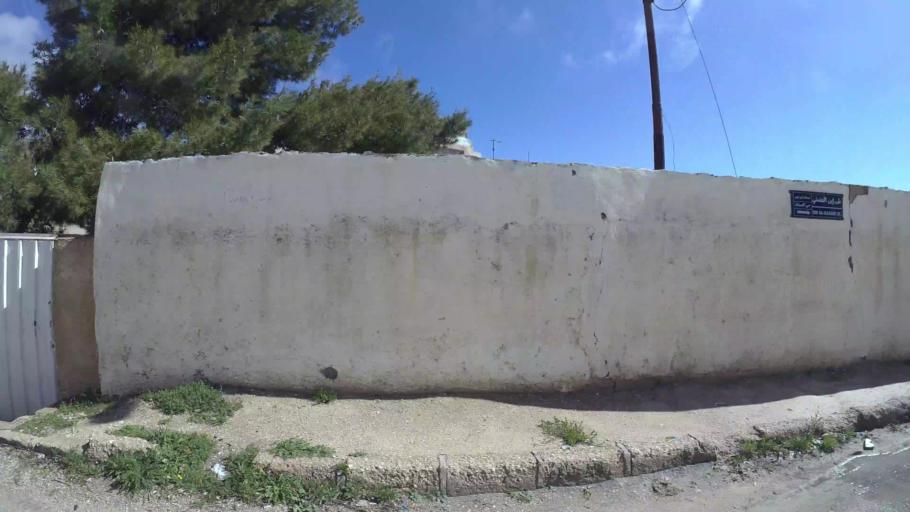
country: JO
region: Amman
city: Al Jubayhah
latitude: 32.0563
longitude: 35.8827
